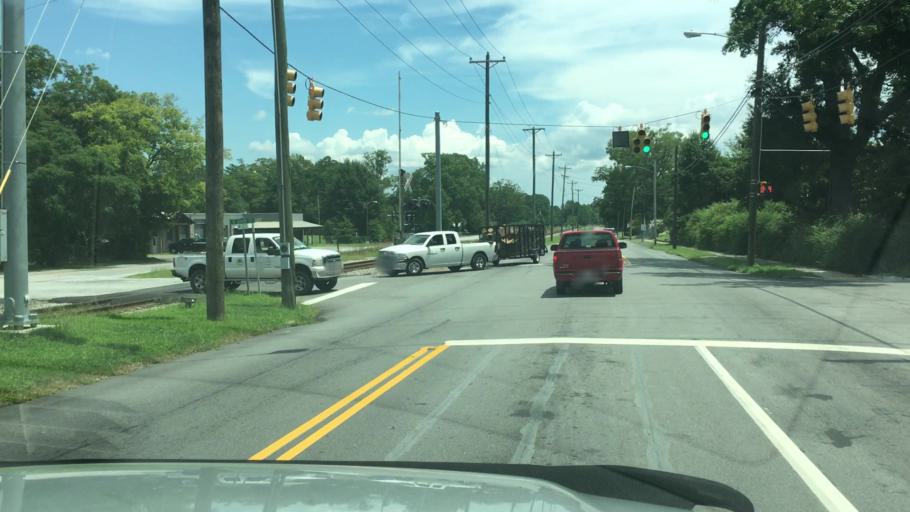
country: US
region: South Carolina
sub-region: Laurens County
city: Clinton
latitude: 34.4717
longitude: -81.8743
